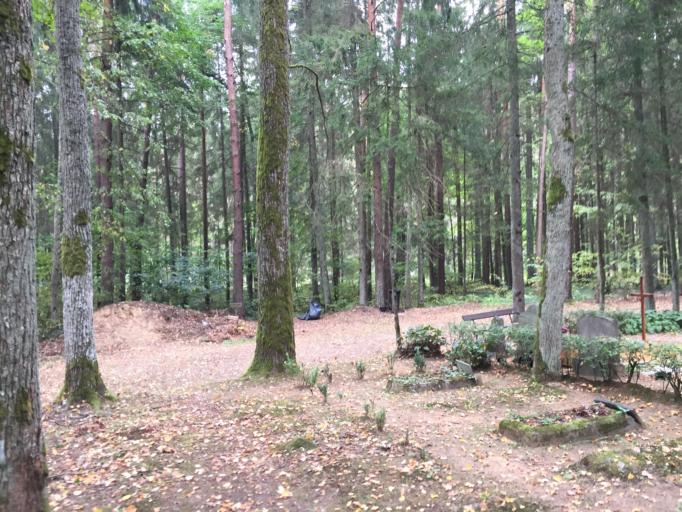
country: LV
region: Baldone
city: Baldone
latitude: 56.7467
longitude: 24.4616
